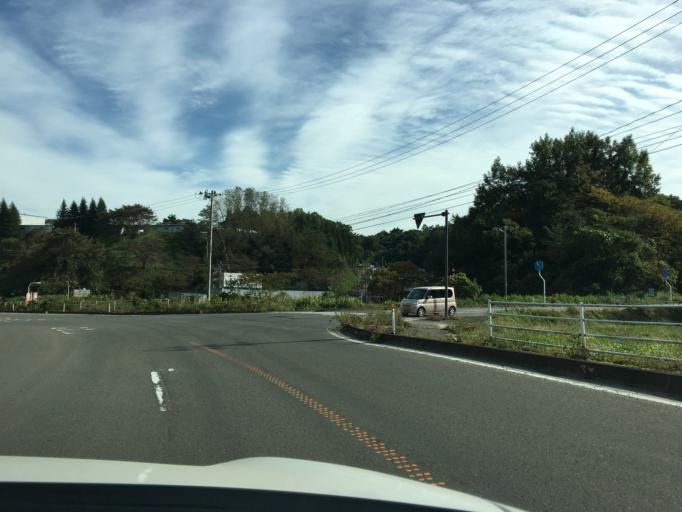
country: JP
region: Fukushima
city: Nihommatsu
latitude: 37.5662
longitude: 140.5011
